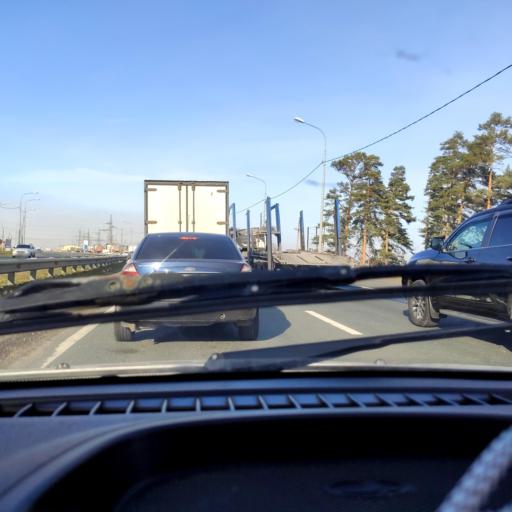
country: RU
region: Samara
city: Zhigulevsk
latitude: 53.5390
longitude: 49.5161
